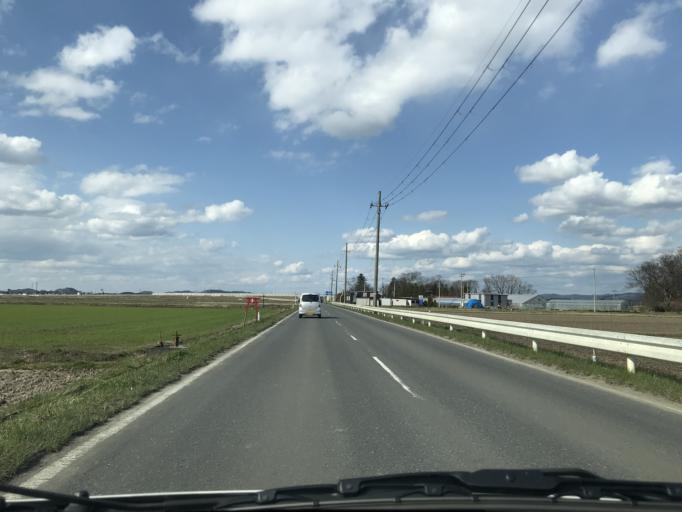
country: JP
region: Miyagi
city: Wakuya
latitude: 38.6798
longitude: 141.2322
